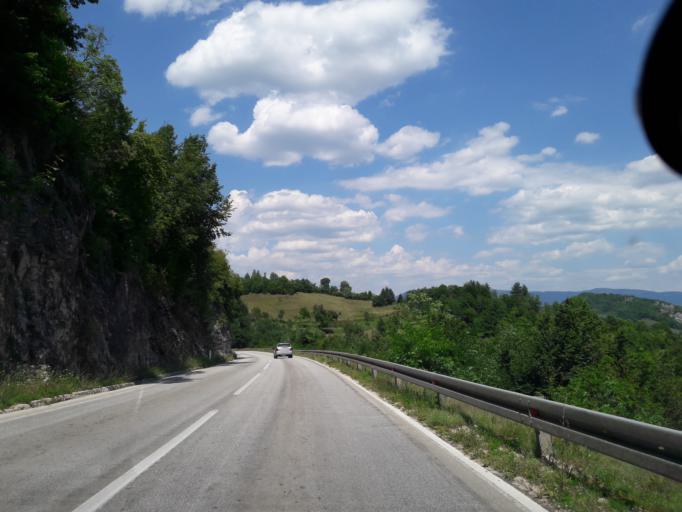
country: BA
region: Republika Srpska
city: Mrkonjic Grad
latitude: 44.4160
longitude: 17.0986
